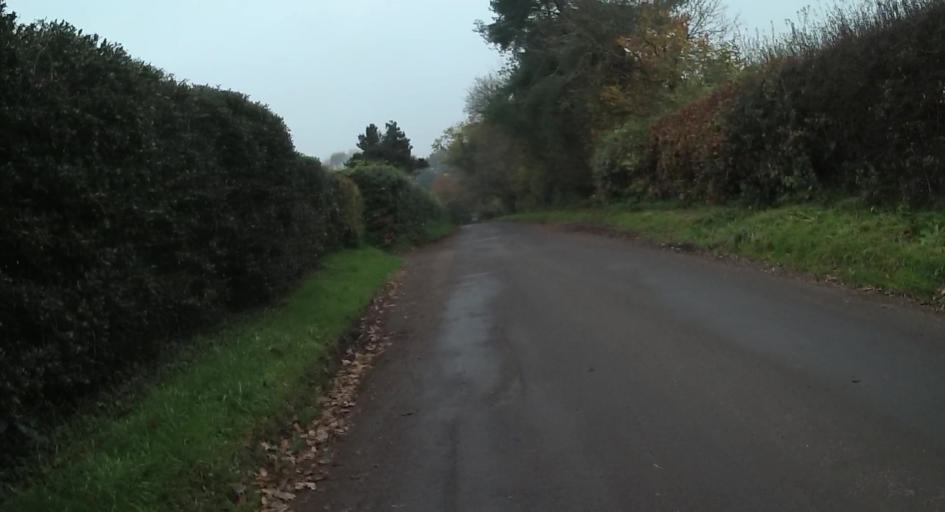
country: GB
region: England
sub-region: Hampshire
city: Old Basing
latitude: 51.2036
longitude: -1.0374
